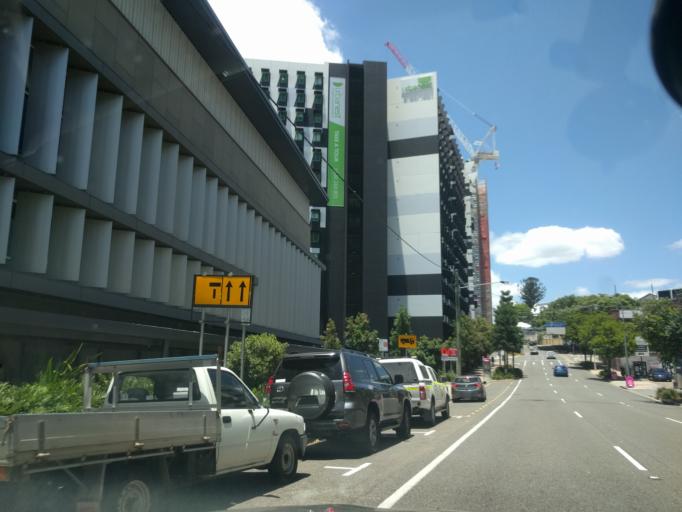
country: AU
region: Queensland
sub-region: Brisbane
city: South Brisbane
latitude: -27.4809
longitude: 153.0205
